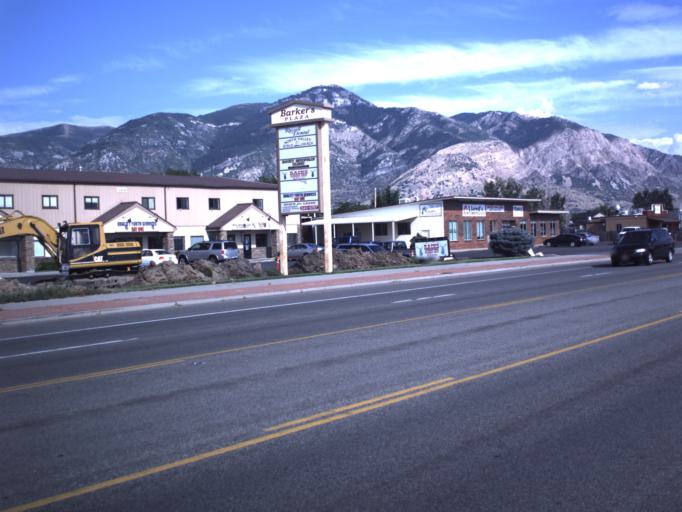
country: US
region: Utah
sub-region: Weber County
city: Harrisville
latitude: 41.2984
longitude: -111.9981
